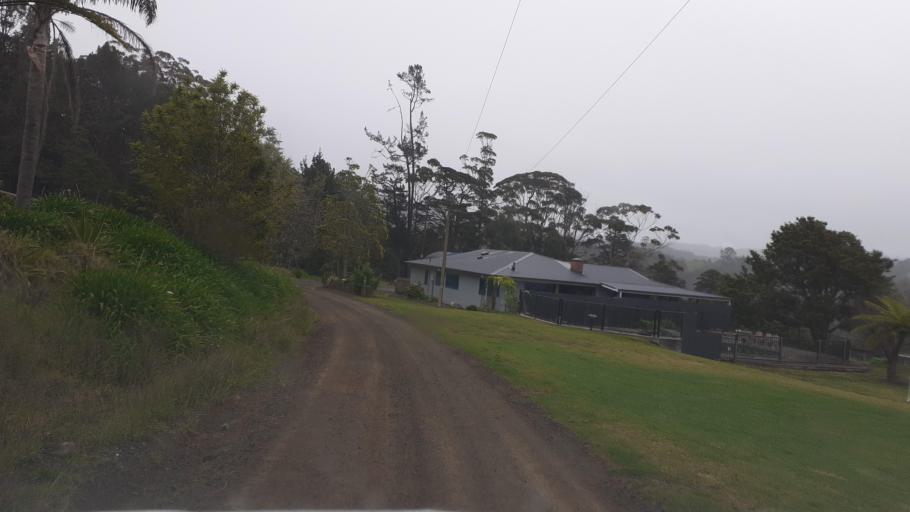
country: NZ
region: Northland
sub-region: Far North District
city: Kerikeri
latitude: -35.1034
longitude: 173.9266
